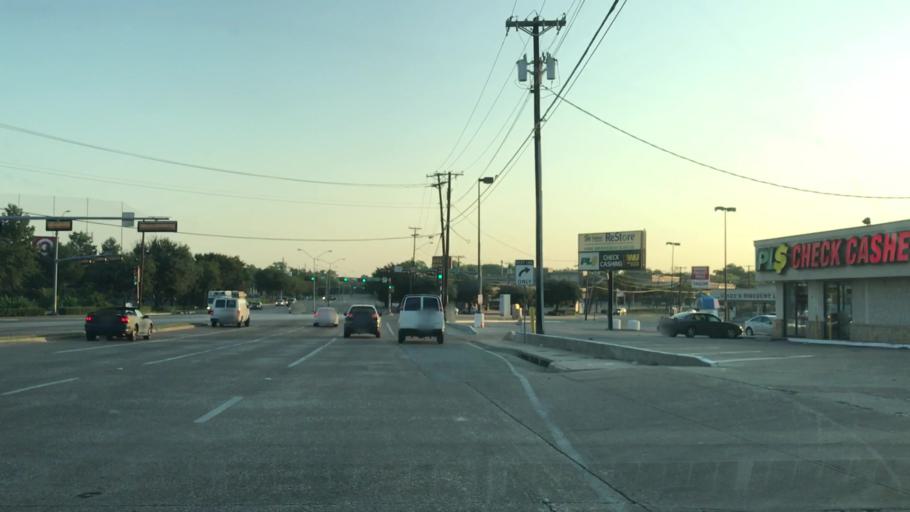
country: US
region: Texas
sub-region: Dallas County
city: Highland Park
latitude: 32.8642
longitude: -96.7438
